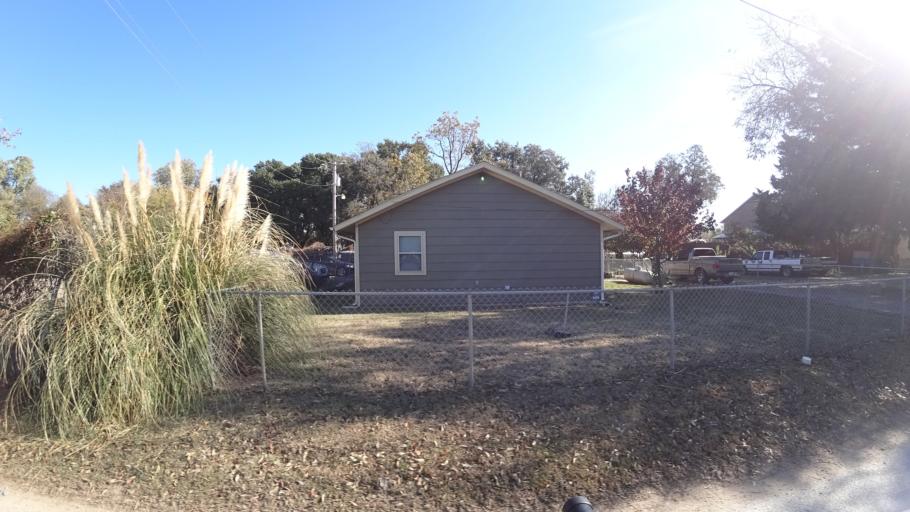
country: US
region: Texas
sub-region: Denton County
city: Lewisville
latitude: 33.0437
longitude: -96.9848
